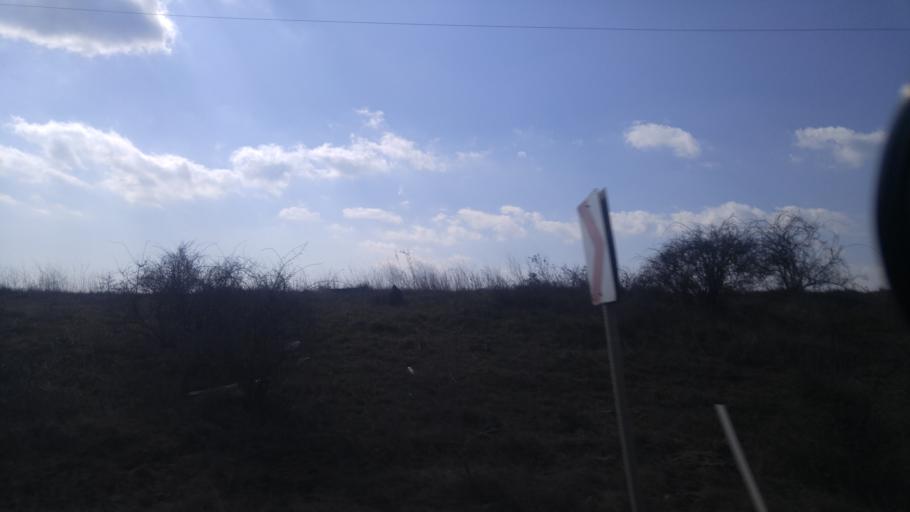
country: TR
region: Istanbul
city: Buyukcavuslu
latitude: 41.1923
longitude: 28.0805
